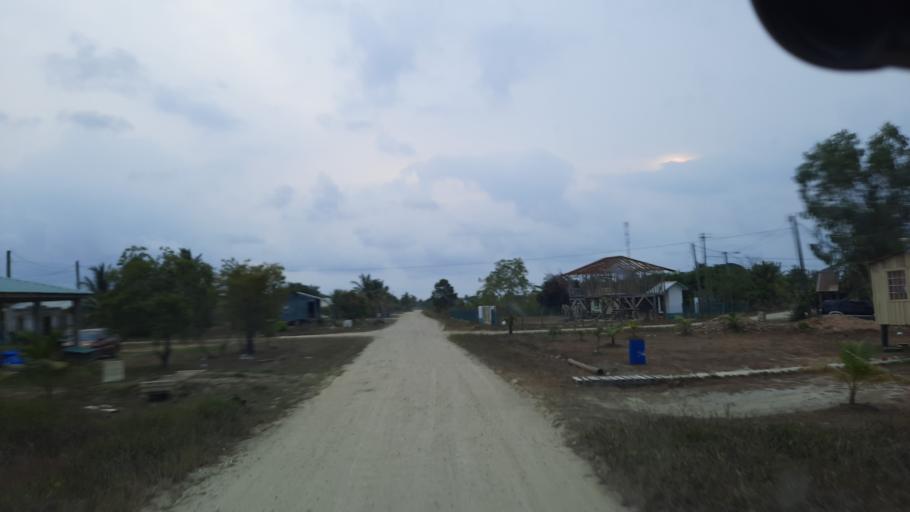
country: BZ
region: Stann Creek
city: Placencia
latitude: 16.5307
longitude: -88.4277
